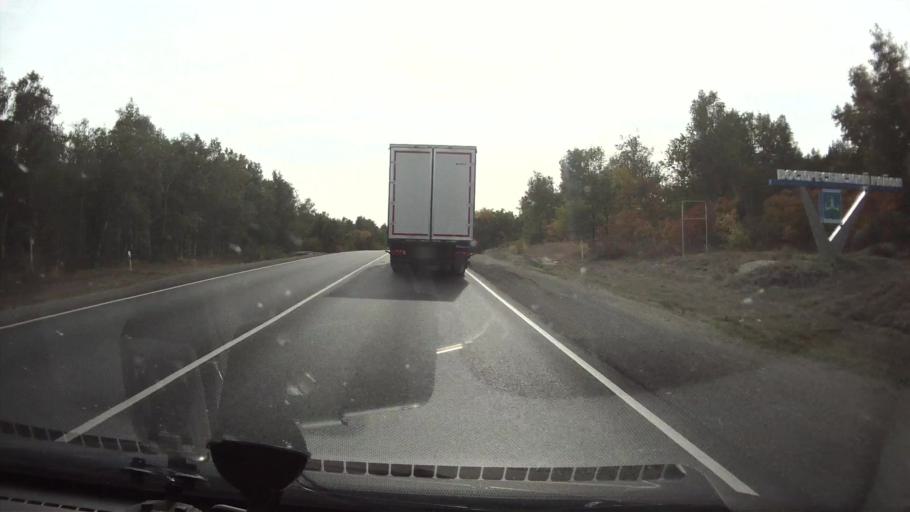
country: RU
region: Saratov
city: Sennoy
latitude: 52.1182
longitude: 46.8413
